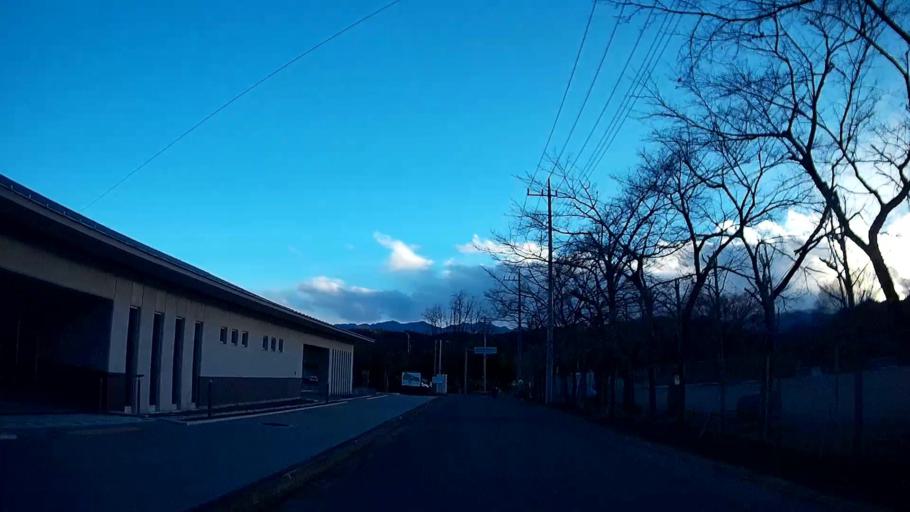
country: JP
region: Saitama
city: Chichibu
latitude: 36.0292
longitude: 138.9874
